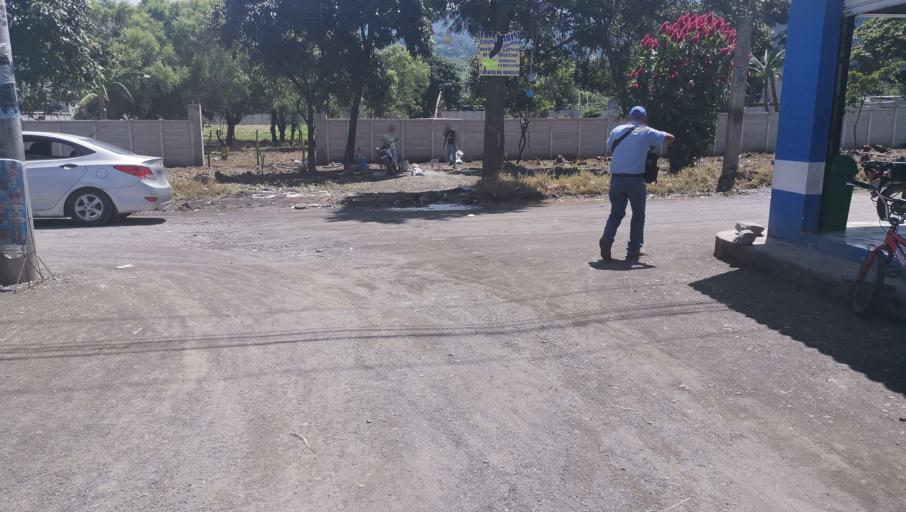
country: GT
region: Escuintla
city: San Vicente Pacaya
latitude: 14.4440
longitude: -90.6340
